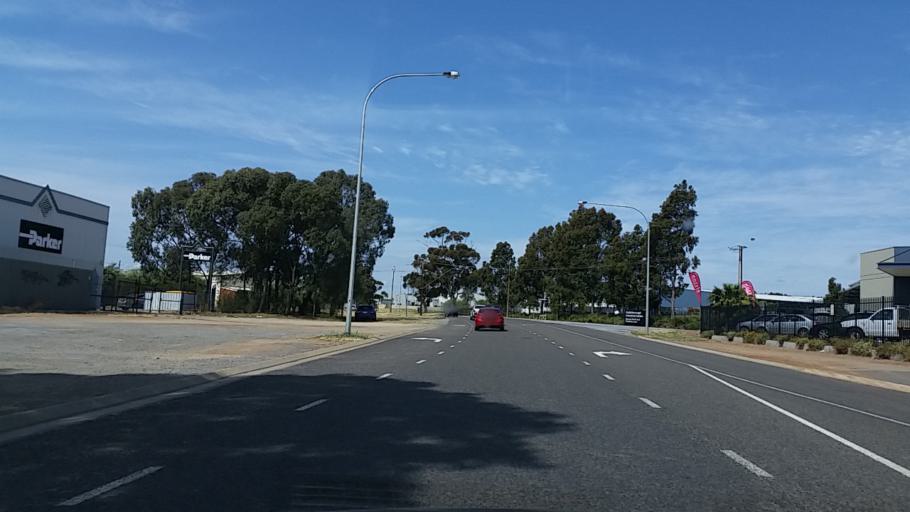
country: AU
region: South Australia
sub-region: Port Adelaide Enfield
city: Enfield
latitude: -34.8315
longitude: 138.6007
